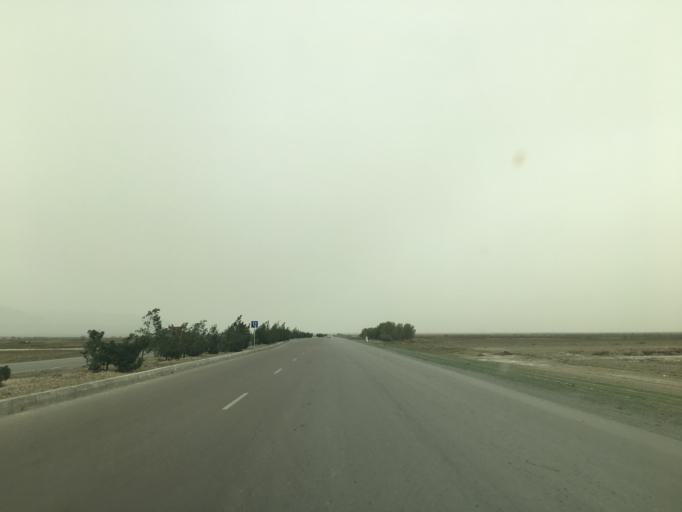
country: TM
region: Ahal
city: Baharly
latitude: 38.3462
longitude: 57.5557
